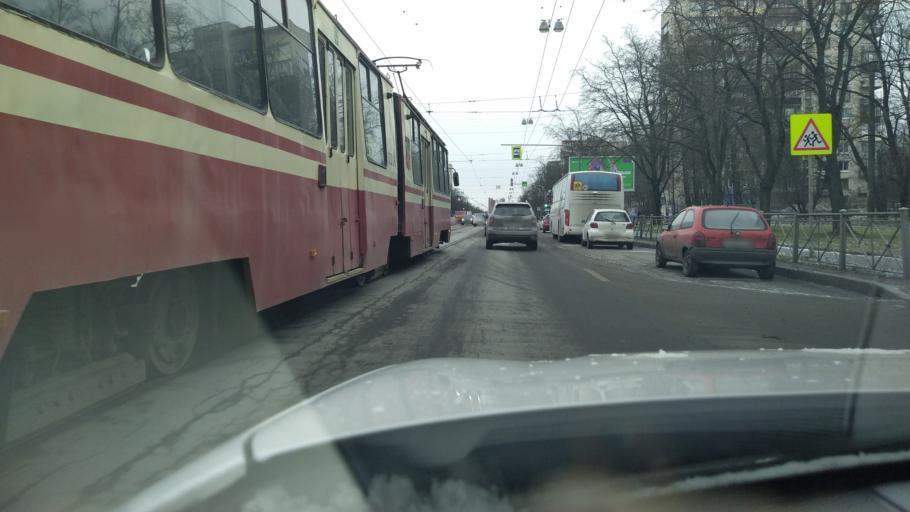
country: RU
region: Leningrad
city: Akademicheskoe
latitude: 60.0089
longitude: 30.4143
